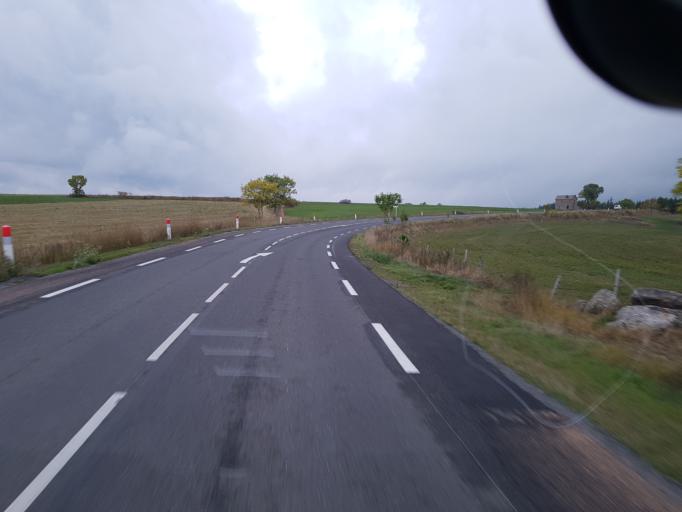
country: FR
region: Languedoc-Roussillon
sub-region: Departement de la Lozere
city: Mende
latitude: 44.5877
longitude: 3.6641
